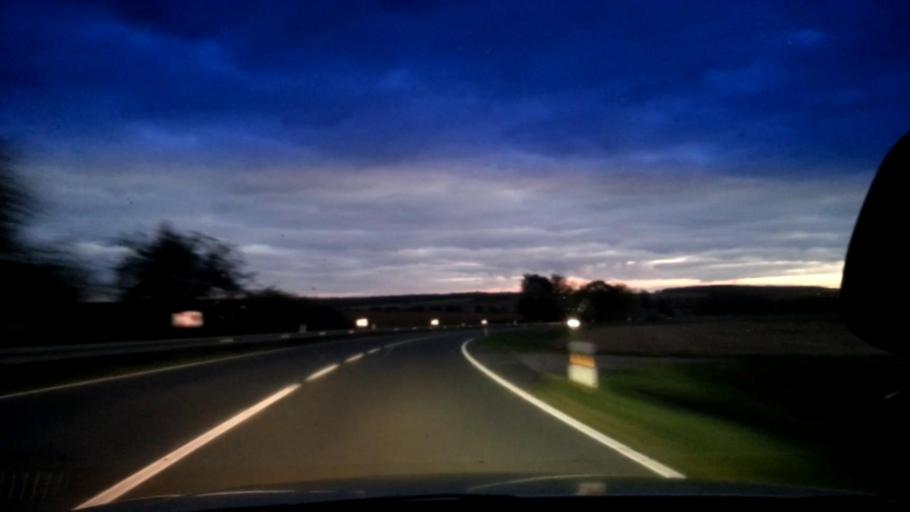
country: DE
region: Bavaria
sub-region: Upper Franconia
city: Memmelsdorf
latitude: 49.9519
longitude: 10.9935
